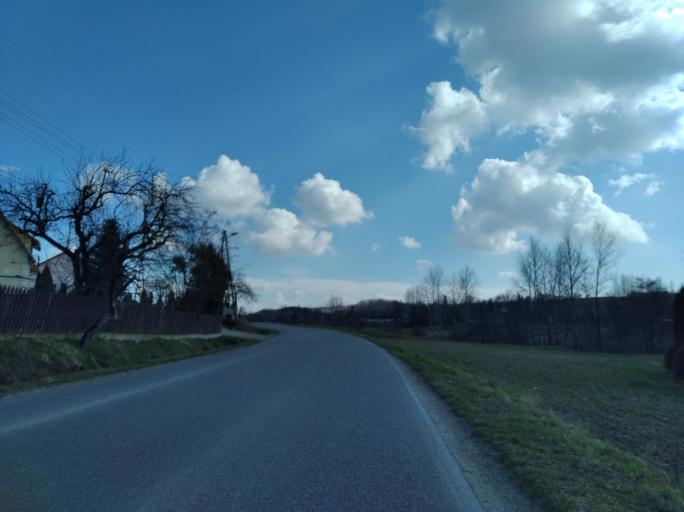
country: PL
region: Subcarpathian Voivodeship
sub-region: Powiat debicki
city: Brzostek
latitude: 49.8609
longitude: 21.4691
